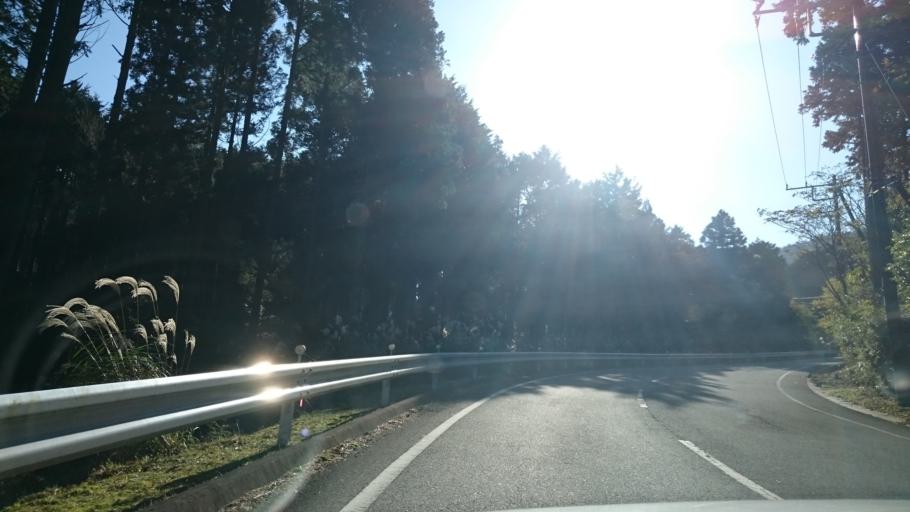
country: JP
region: Shizuoka
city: Heda
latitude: 34.9930
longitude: 138.8125
